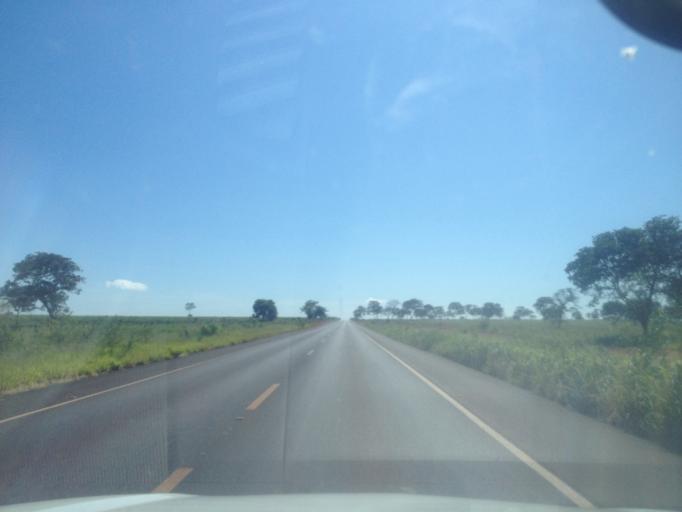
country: BR
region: Minas Gerais
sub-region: Santa Vitoria
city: Santa Vitoria
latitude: -19.0286
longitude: -50.3655
